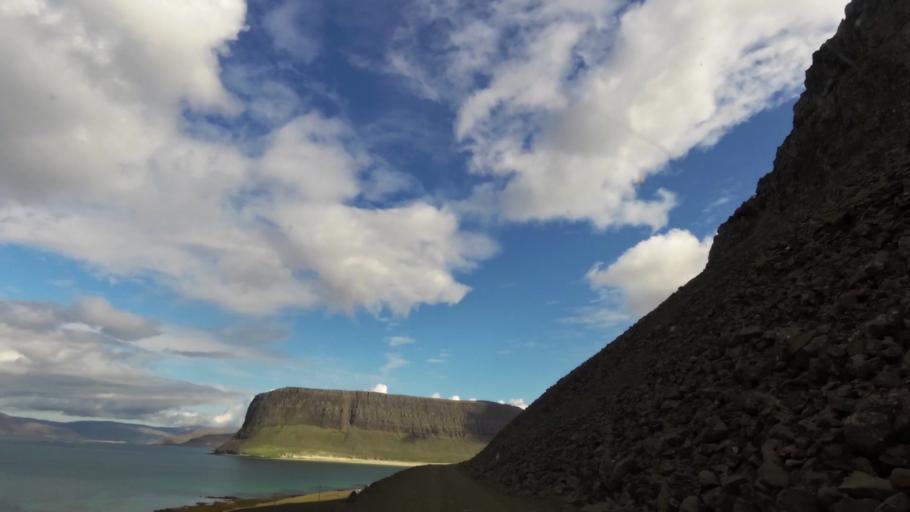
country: IS
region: West
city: Olafsvik
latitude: 65.5965
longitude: -24.1315
